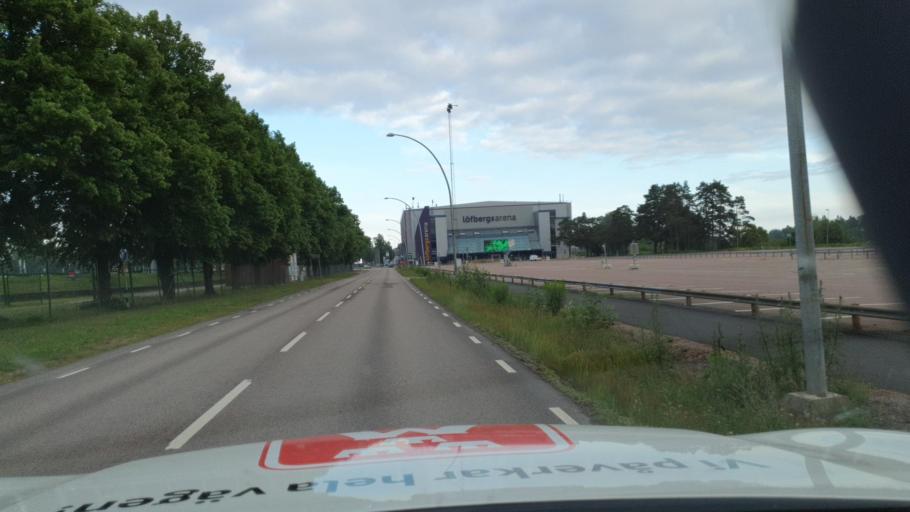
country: SE
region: Vaermland
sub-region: Karlstads Kommun
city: Karlstad
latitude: 59.4101
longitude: 13.4972
